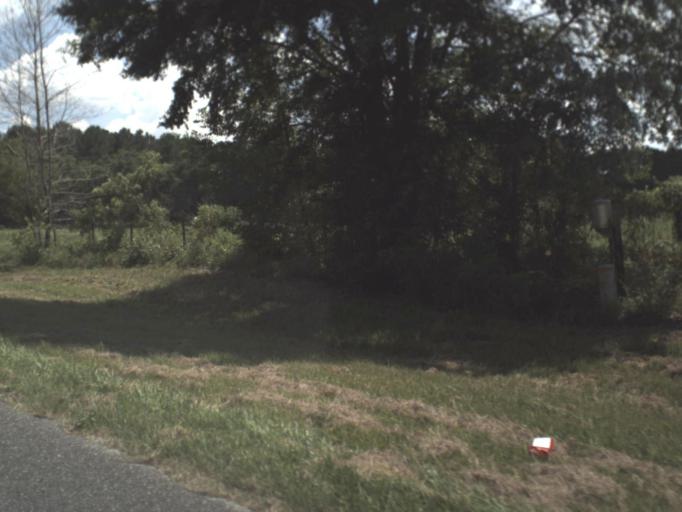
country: US
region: Florida
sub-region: Alachua County
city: High Springs
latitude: 29.9098
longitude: -82.6095
